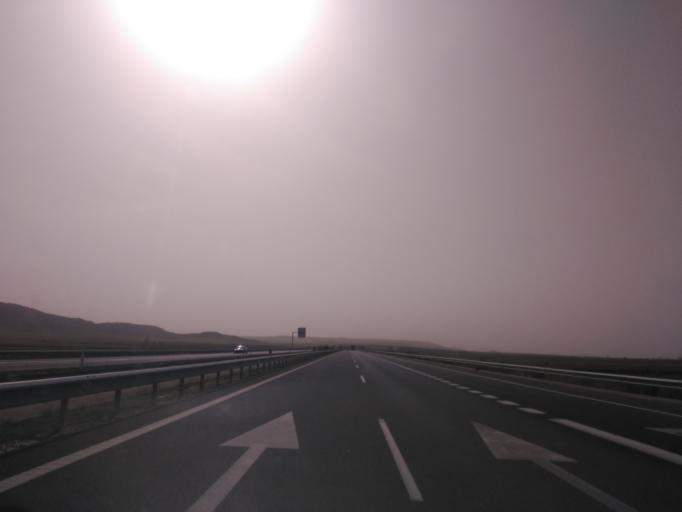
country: ES
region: Castille and Leon
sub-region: Provincia de Palencia
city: Amusco
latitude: 42.1871
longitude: -4.4497
